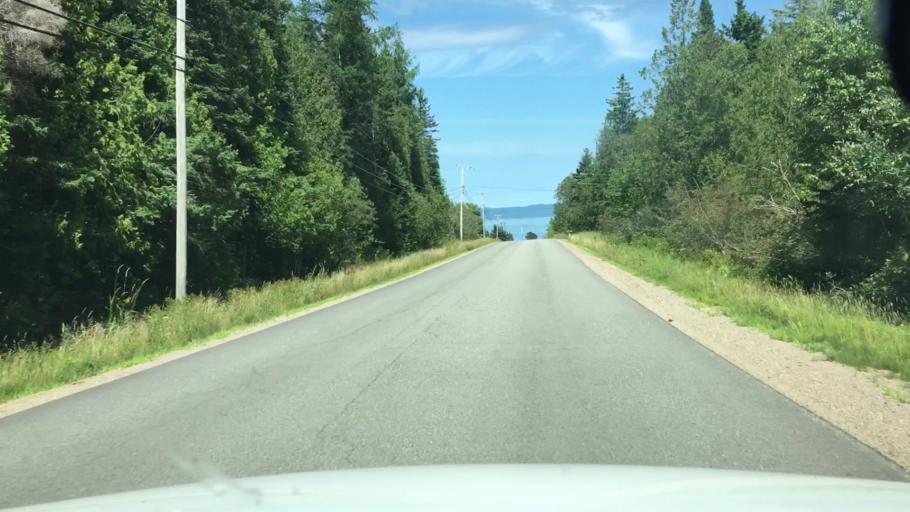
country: CA
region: New Brunswick
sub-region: Charlotte County
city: Saint Andrews
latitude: 44.9886
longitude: -67.0686
